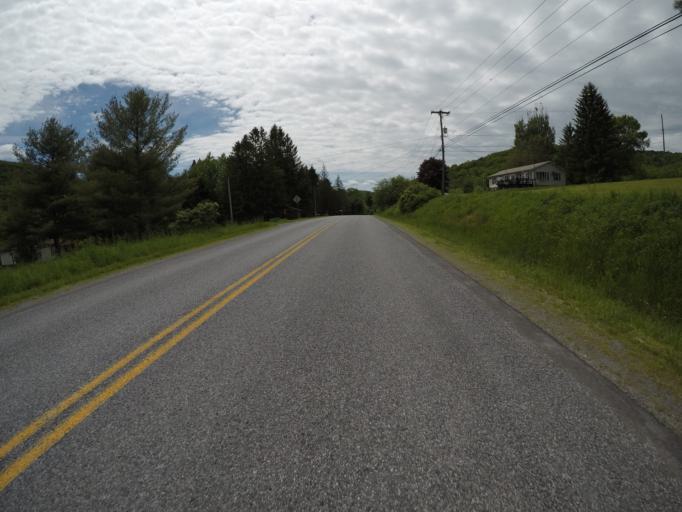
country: US
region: New York
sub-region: Delaware County
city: Stamford
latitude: 42.2049
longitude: -74.5742
